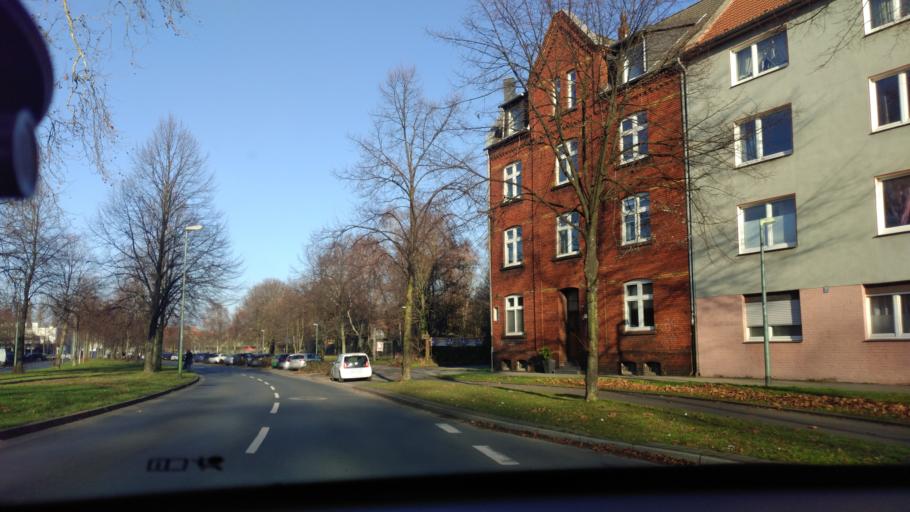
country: DE
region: North Rhine-Westphalia
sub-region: Regierungsbezirk Dusseldorf
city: Essen
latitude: 51.4939
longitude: 7.0108
